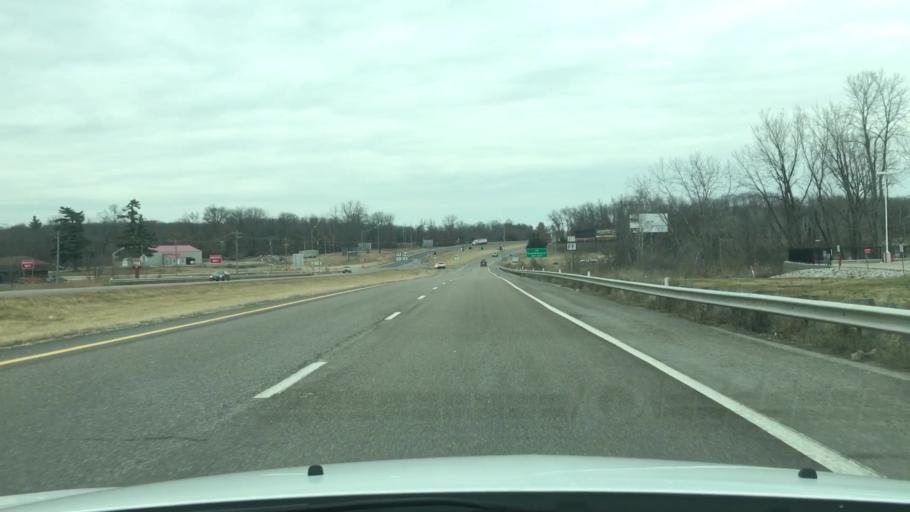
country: US
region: Missouri
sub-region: Callaway County
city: Fulton
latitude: 38.9466
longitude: -91.9408
